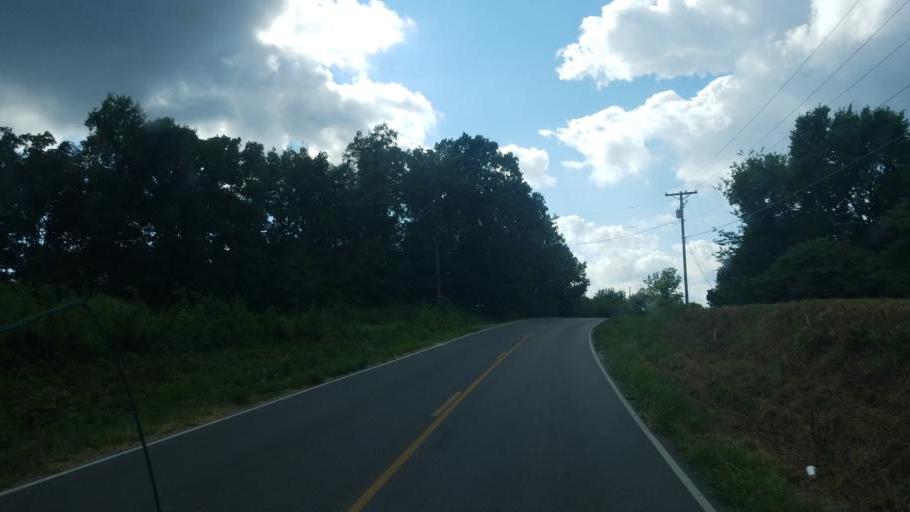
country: US
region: Illinois
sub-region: Union County
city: Cobden
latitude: 37.5574
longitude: -89.3023
